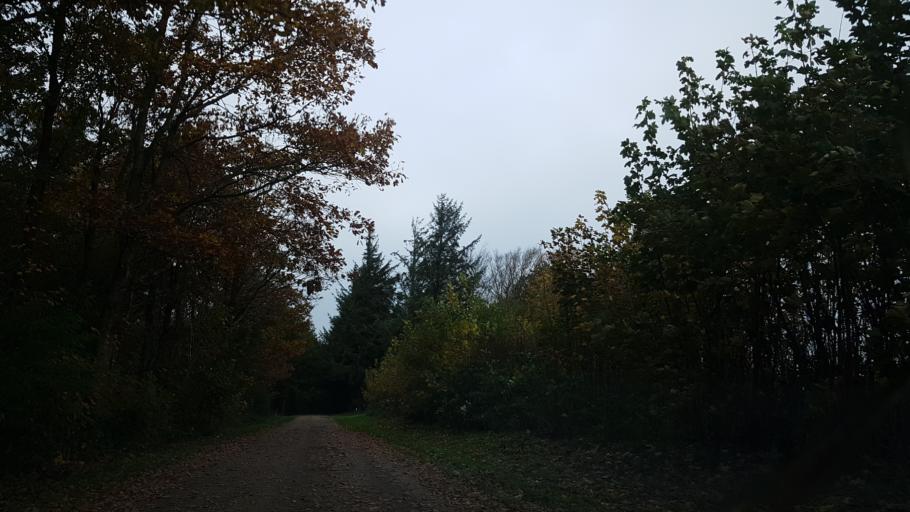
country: DK
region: South Denmark
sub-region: Tonder Kommune
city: Sherrebek
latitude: 55.1719
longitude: 8.7653
